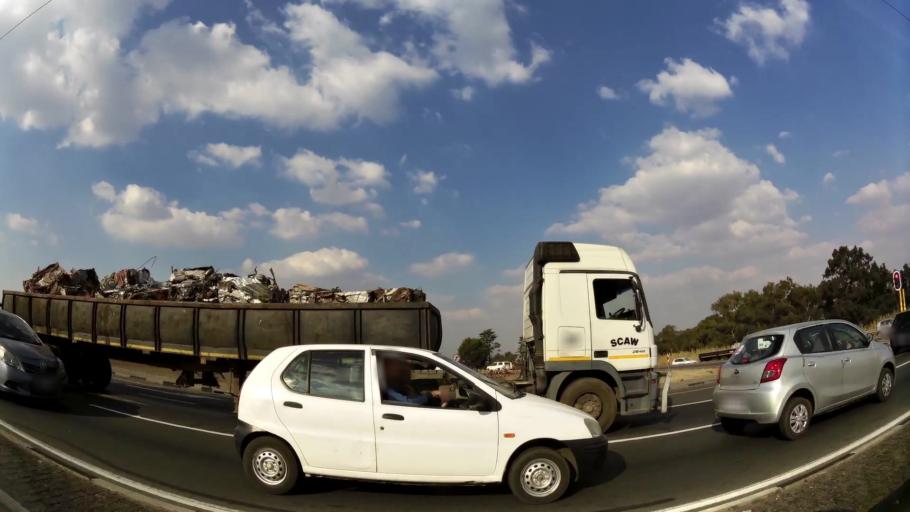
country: ZA
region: Gauteng
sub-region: Ekurhuleni Metropolitan Municipality
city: Germiston
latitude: -26.2501
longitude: 28.1630
